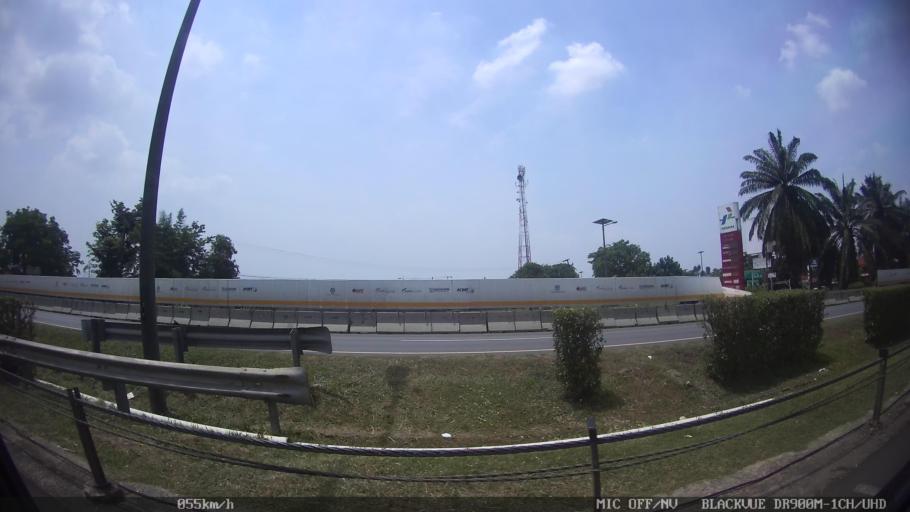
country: ID
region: Banten
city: Serang
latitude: -6.1317
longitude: 106.2029
